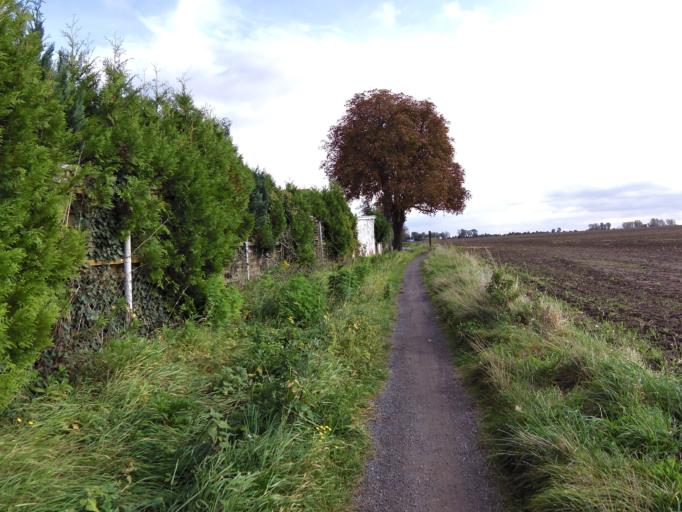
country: DE
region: Saxony
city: Markkleeberg
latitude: 51.2846
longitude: 12.4335
